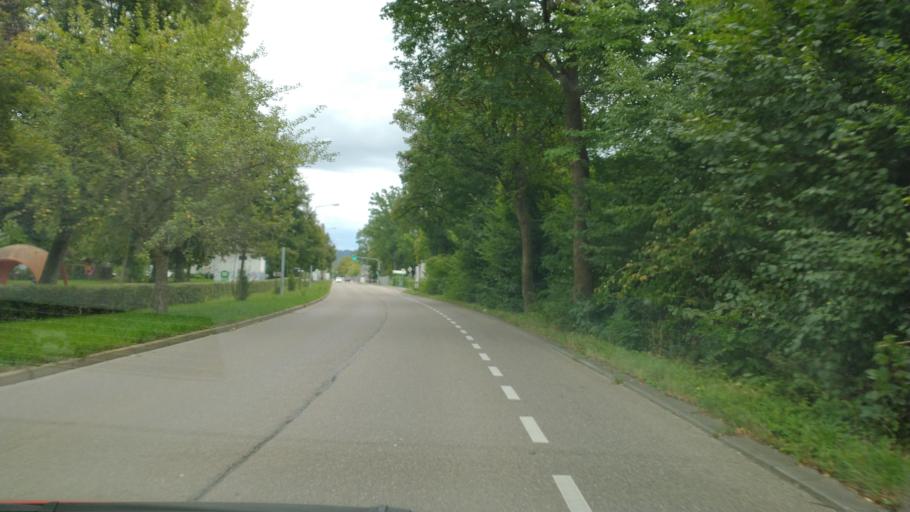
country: DE
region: Baden-Wuerttemberg
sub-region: Regierungsbezirk Stuttgart
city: Schwabisch Gmund
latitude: 48.7951
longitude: 9.8188
